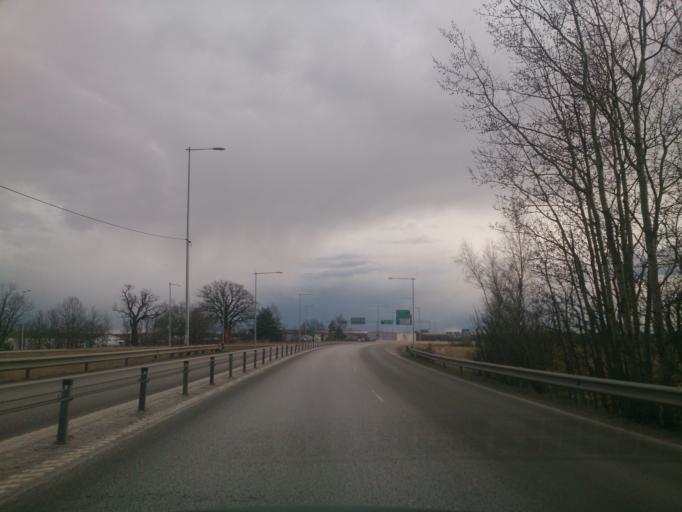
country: SE
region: OEstergoetland
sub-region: Norrkopings Kommun
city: Jursla
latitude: 58.6567
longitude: 16.1703
